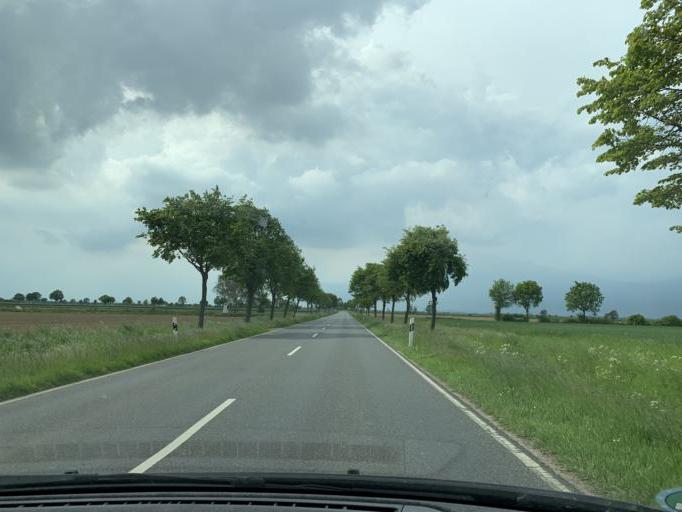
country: DE
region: North Rhine-Westphalia
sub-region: Regierungsbezirk Koln
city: Vettweiss
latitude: 50.7431
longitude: 6.5859
